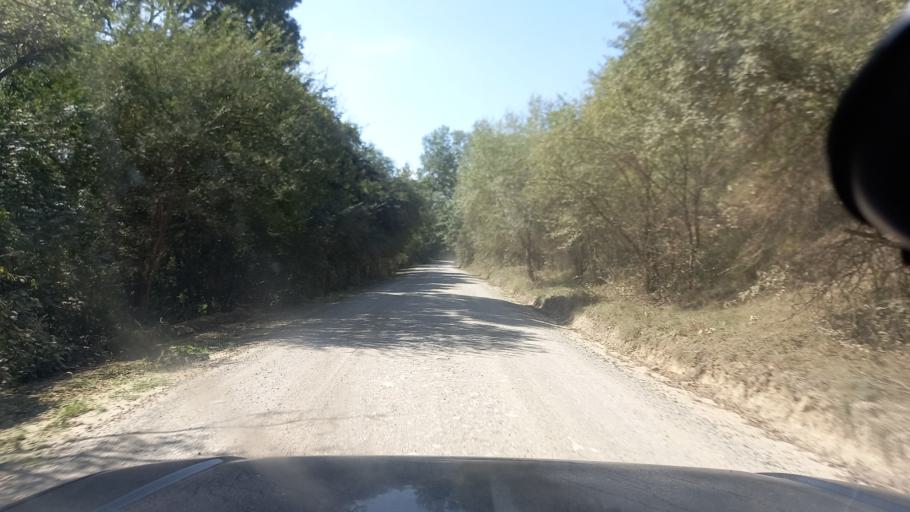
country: RU
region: Krasnodarskiy
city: Azovskaya
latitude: 44.6986
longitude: 38.6628
